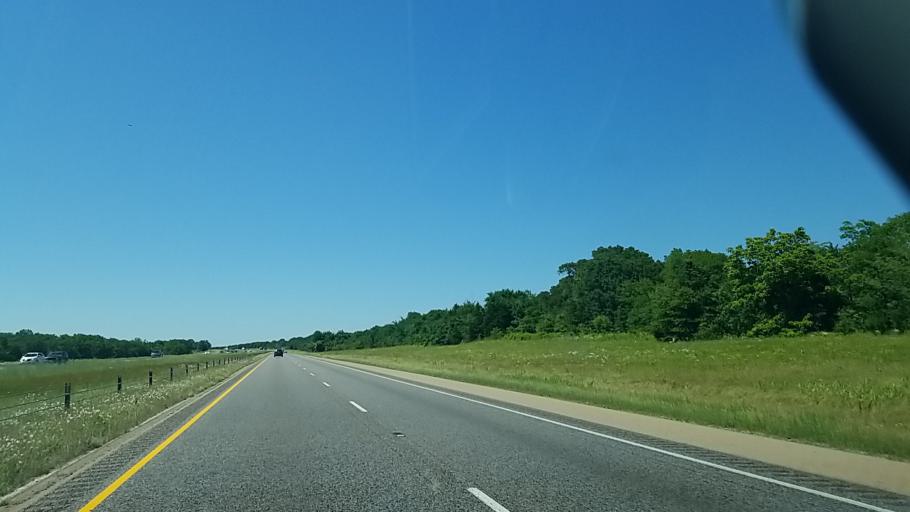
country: US
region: Texas
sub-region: Freestone County
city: Fairfield
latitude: 31.6800
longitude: -96.1647
